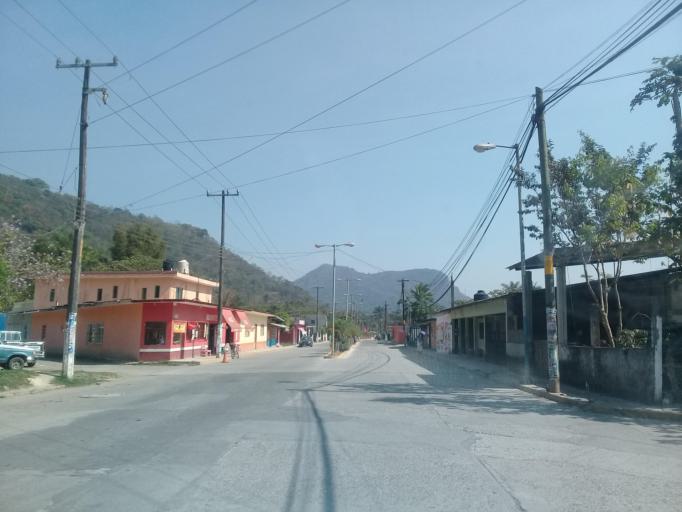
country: MX
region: Veracruz
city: Rafael Delgado
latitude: 18.7837
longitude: -97.0125
